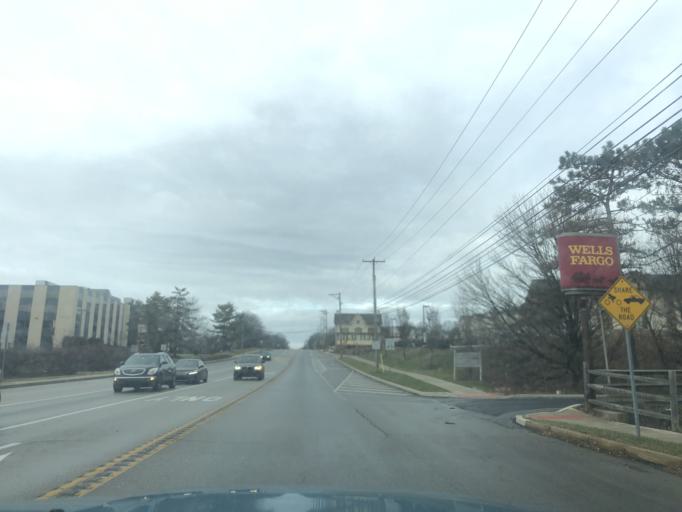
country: US
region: Pennsylvania
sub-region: Montgomery County
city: Dresher
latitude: 40.1423
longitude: -75.1690
